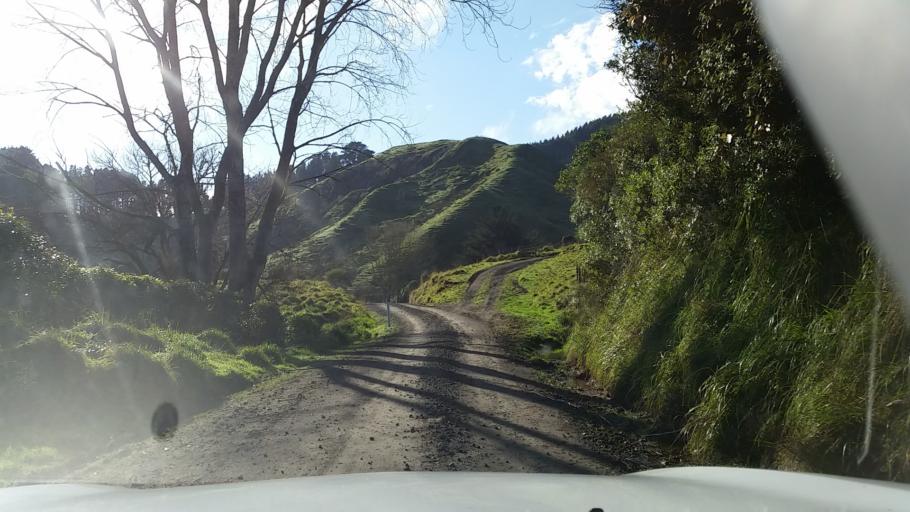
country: NZ
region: Taranaki
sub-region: South Taranaki District
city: Eltham
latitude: -39.5111
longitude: 174.3952
